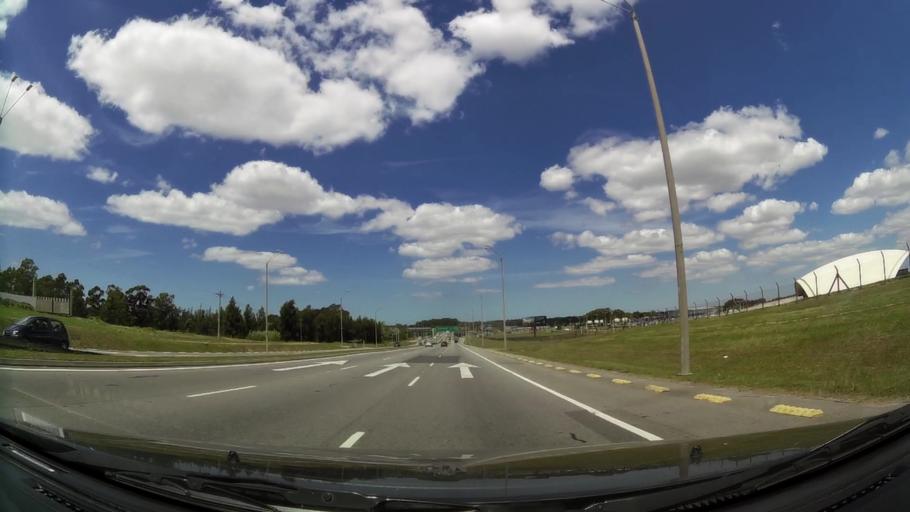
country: UY
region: Canelones
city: Colonia Nicolich
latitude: -34.8350
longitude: -56.0121
